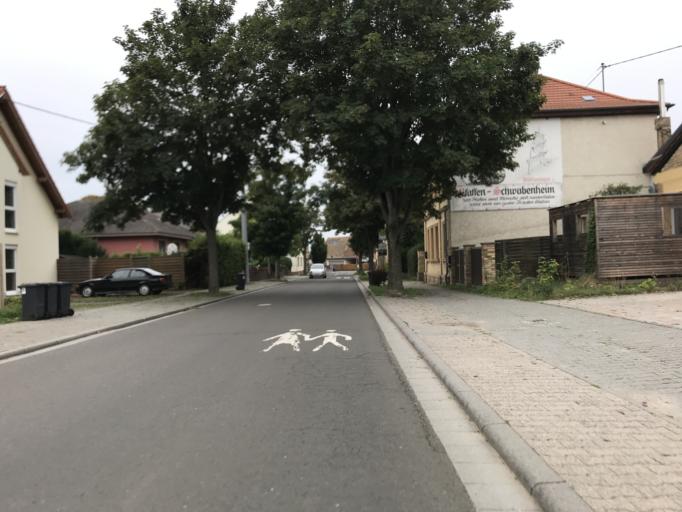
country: DE
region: Rheinland-Pfalz
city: Pfaffen-Schwabenheim
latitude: 49.8533
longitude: 7.9533
